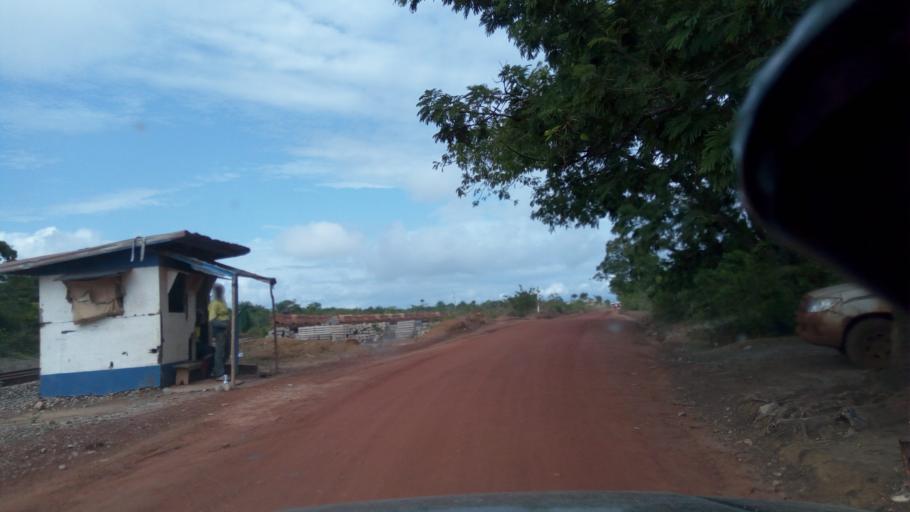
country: SL
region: Northern Province
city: Pepel
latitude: 8.6024
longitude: -13.0528
